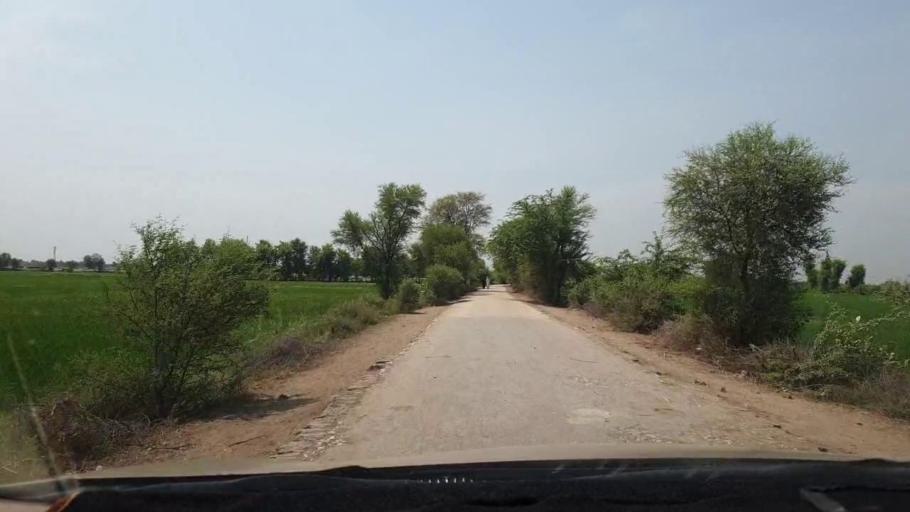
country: PK
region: Sindh
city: Larkana
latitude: 27.6286
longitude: 68.2738
